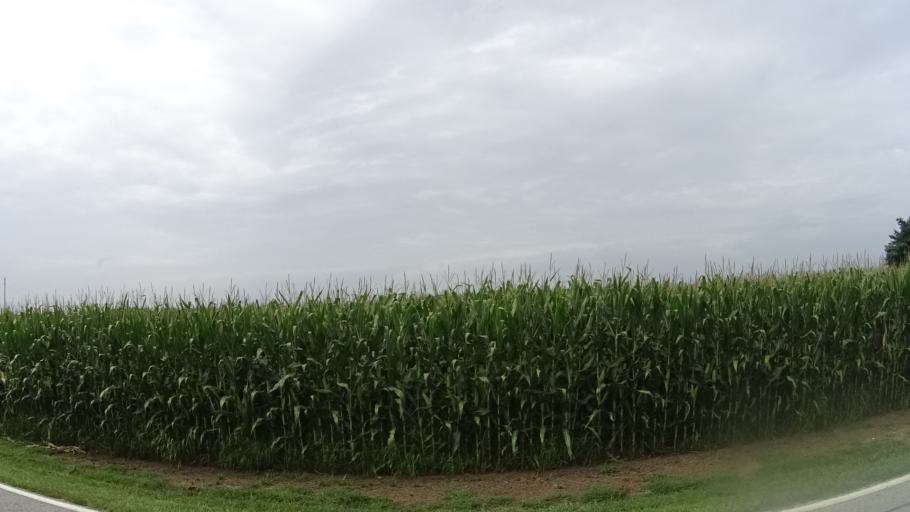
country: US
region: Indiana
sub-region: Madison County
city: Pendleton
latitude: 40.0330
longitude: -85.7919
